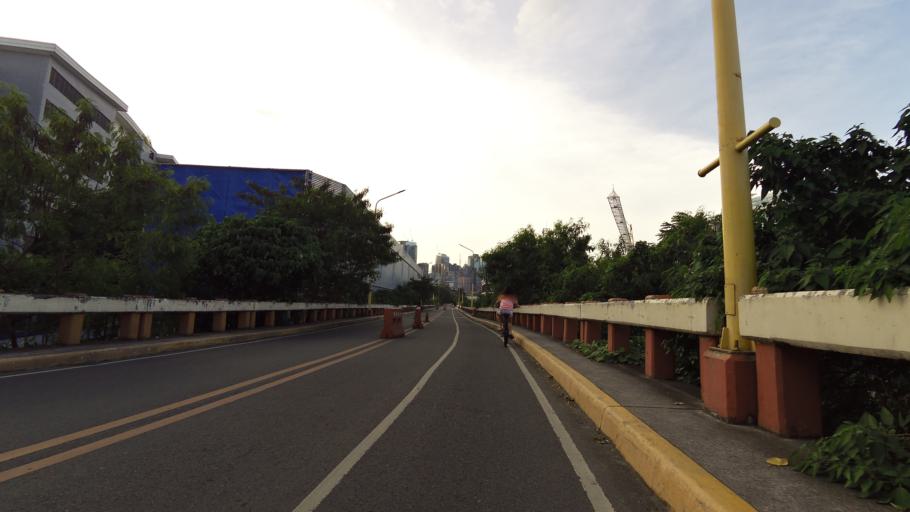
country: PH
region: Metro Manila
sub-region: Pasig
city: Pasig City
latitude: 14.5756
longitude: 121.0757
